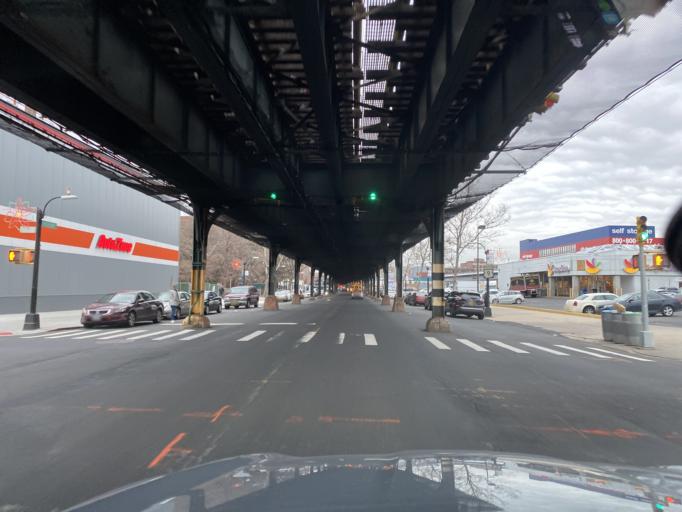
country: US
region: New York
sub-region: New York County
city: Inwood
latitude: 40.8816
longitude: -73.9029
